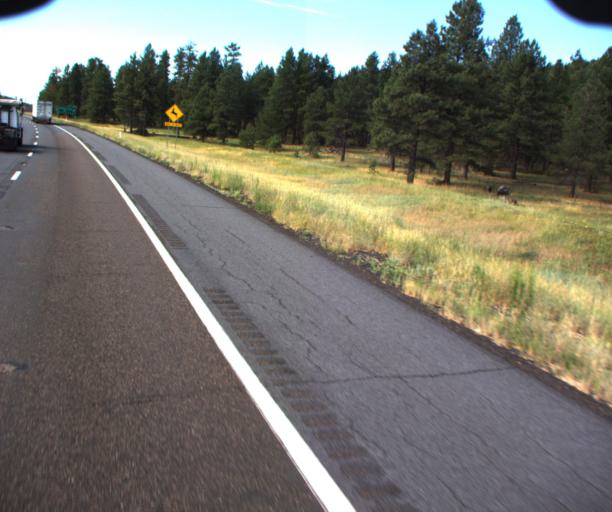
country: US
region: Arizona
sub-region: Coconino County
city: Mountainaire
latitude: 35.0231
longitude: -111.6858
